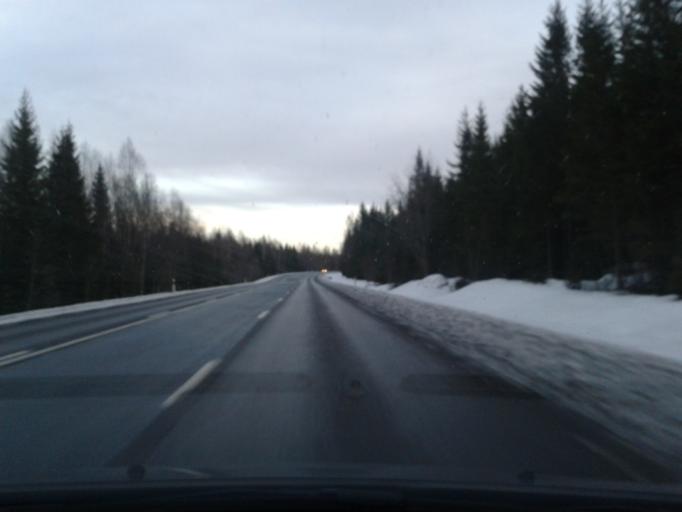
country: SE
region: Vaesternorrland
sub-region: Solleftea Kommun
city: Solleftea
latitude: 63.1407
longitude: 17.4264
